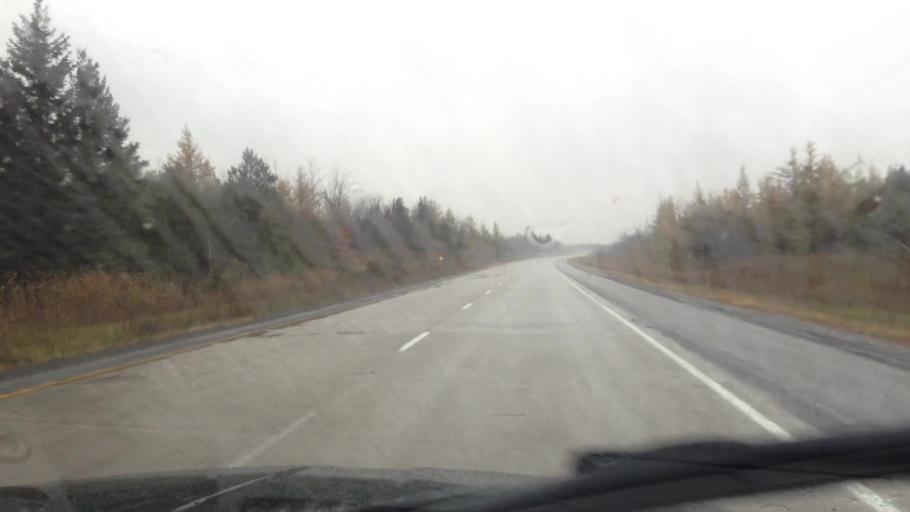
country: CA
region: Ontario
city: Hawkesbury
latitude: 45.4870
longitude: -74.6298
